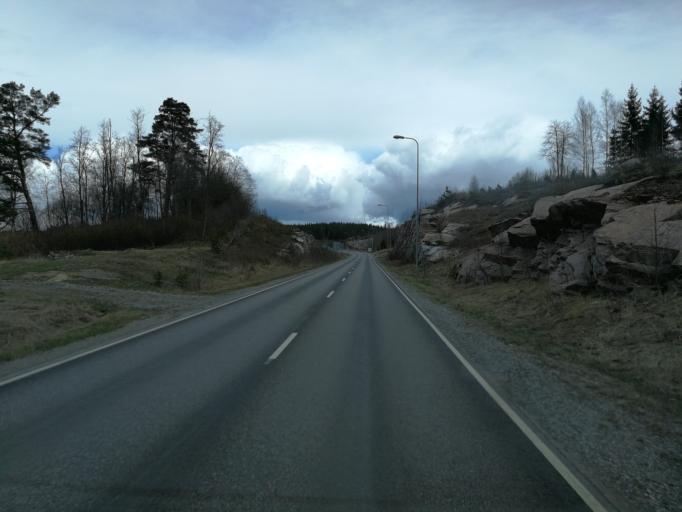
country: FI
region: Varsinais-Suomi
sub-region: Salo
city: Muurla
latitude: 60.3760
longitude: 23.3168
